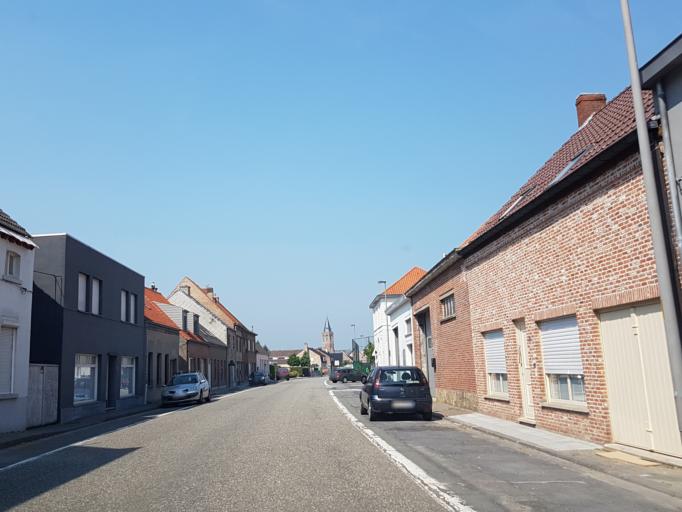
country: BE
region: Flanders
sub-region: Provincie West-Vlaanderen
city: Jabbeke
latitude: 51.2100
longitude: 3.0759
